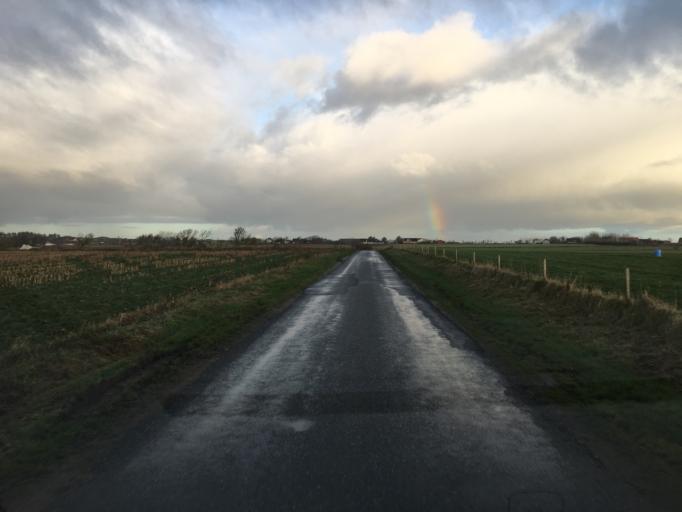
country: DK
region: South Denmark
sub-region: Tonder Kommune
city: Sherrebek
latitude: 55.1483
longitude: 8.8266
